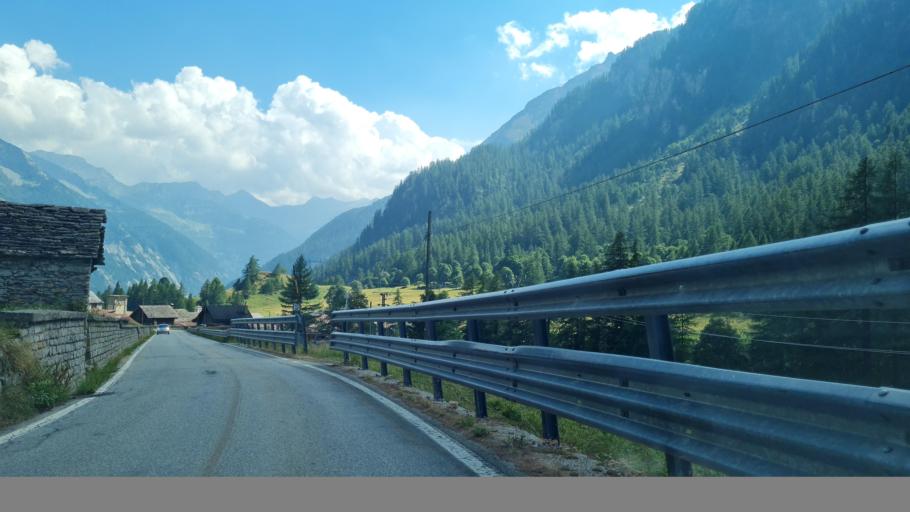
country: IT
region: Piedmont
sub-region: Provincia Verbano-Cusio-Ossola
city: Formazza
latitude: 46.3946
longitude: 8.4194
